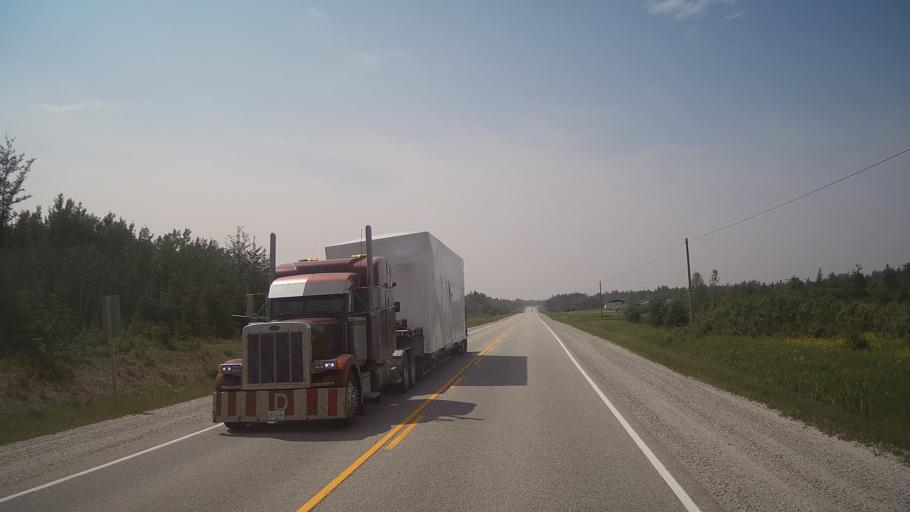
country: CA
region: Ontario
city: Kapuskasing
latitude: 49.2831
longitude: -81.7584
